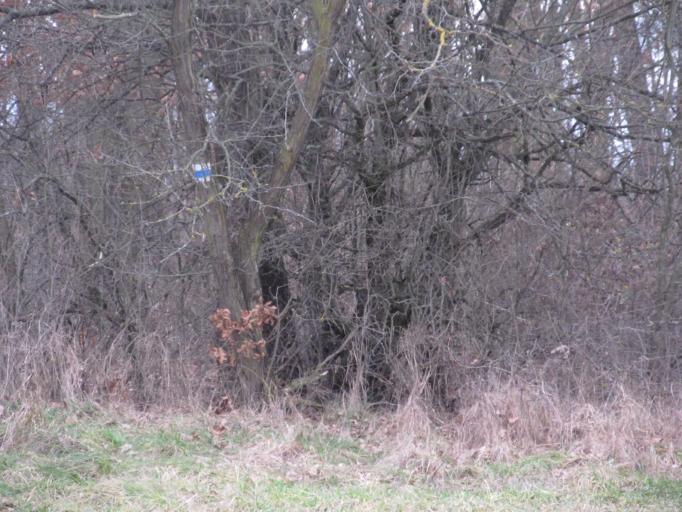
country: HU
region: Vas
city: Sarvar
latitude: 47.2389
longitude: 17.0065
